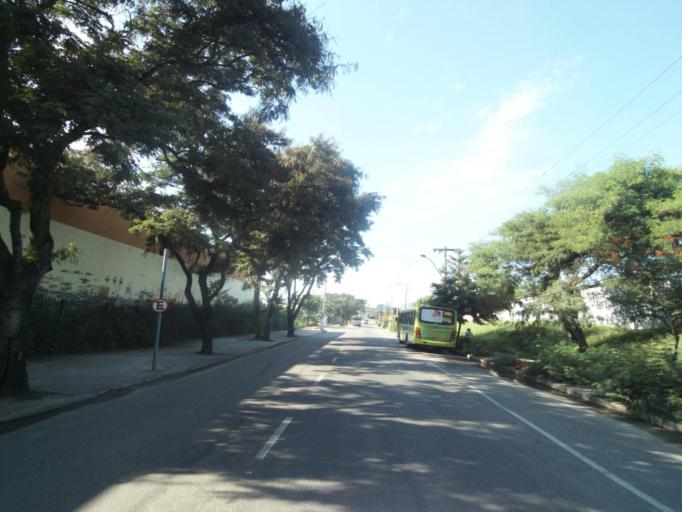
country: BR
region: Rio de Janeiro
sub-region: Niteroi
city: Niteroi
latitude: -22.8870
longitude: -43.1276
